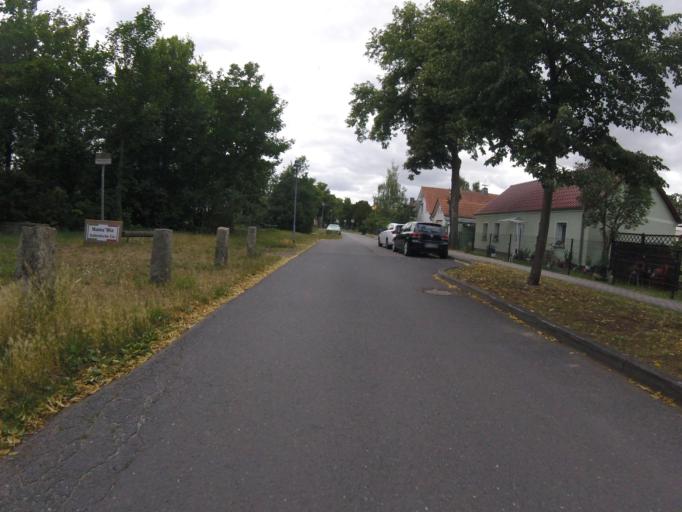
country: DE
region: Brandenburg
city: Konigs Wusterhausen
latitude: 52.2993
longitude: 13.6558
